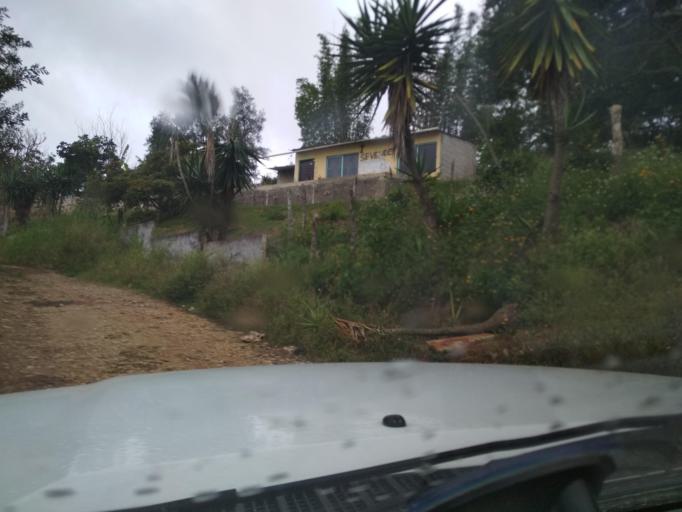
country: MX
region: Veracruz
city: El Castillo
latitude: 19.5382
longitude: -96.8289
